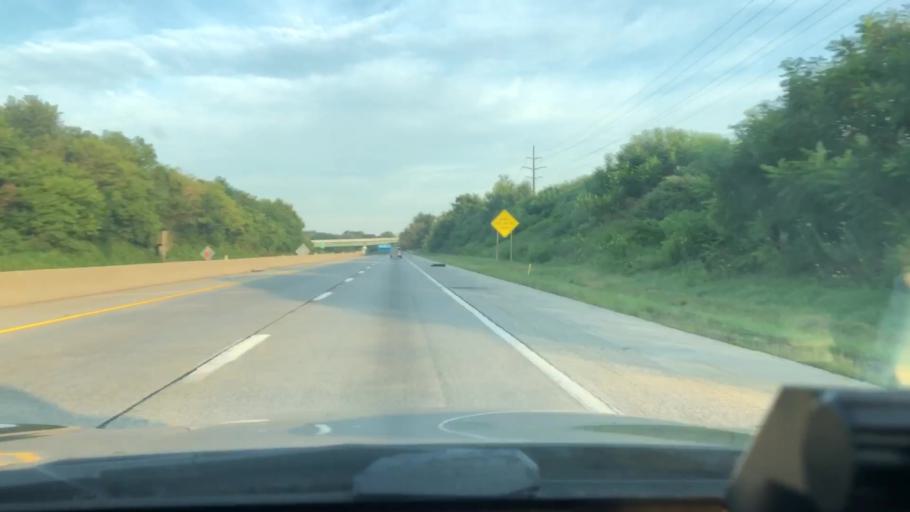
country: US
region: Pennsylvania
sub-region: Lehigh County
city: Wescosville
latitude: 40.5882
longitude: -75.5844
